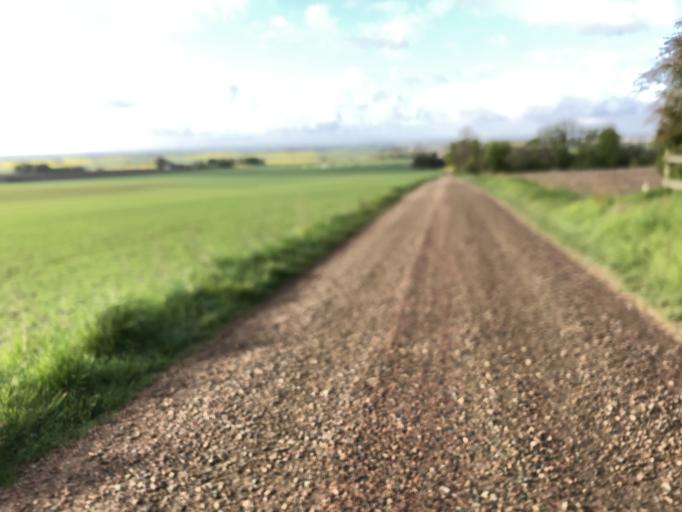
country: SE
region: Skane
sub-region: Lunds Kommun
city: Lund
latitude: 55.6919
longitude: 13.2712
